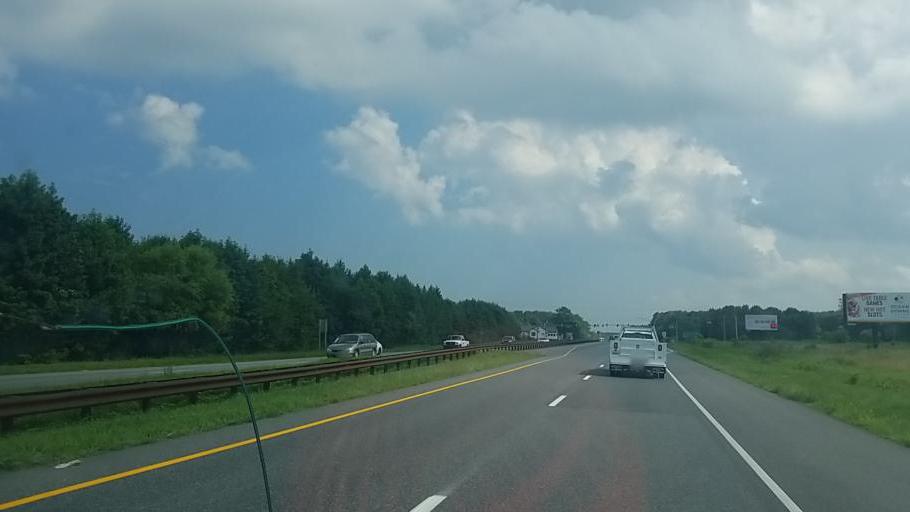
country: US
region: Delaware
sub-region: Sussex County
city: Selbyville
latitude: 38.4309
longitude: -75.2210
